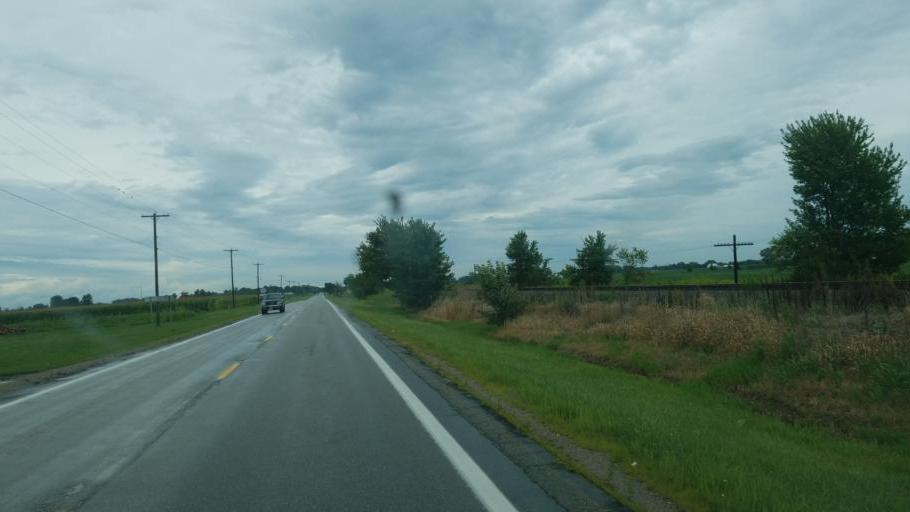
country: US
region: Ohio
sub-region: Delaware County
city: Ashley
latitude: 40.3865
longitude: -82.9702
